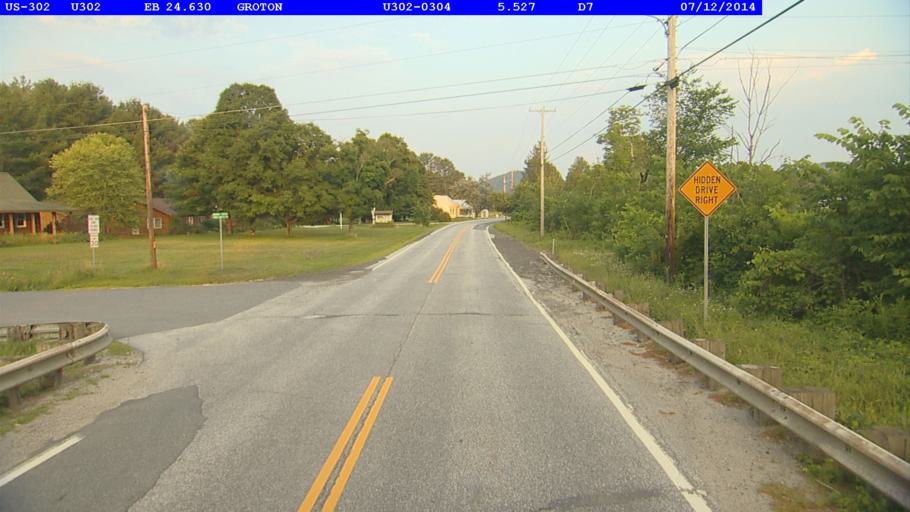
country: US
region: New Hampshire
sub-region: Grafton County
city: Woodsville
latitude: 44.2174
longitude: -72.2122
